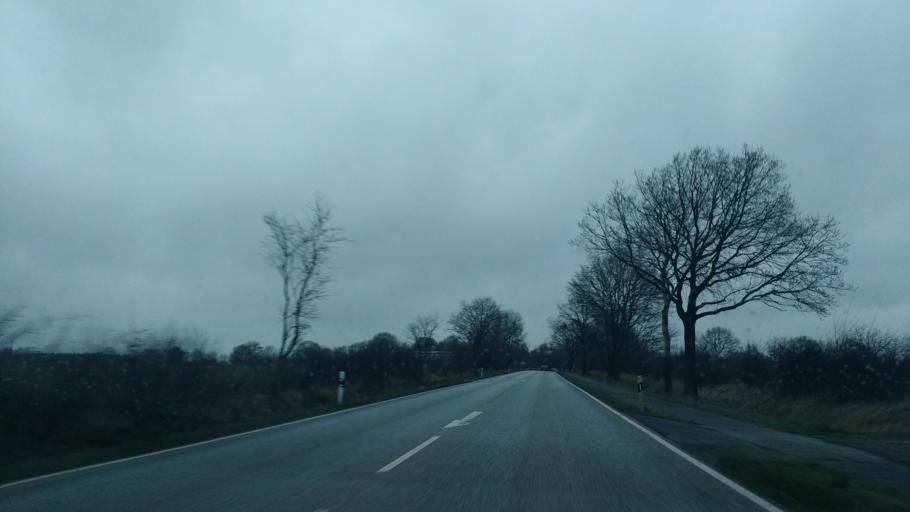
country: DE
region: Schleswig-Holstein
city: Peissen
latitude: 54.0248
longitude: 9.5941
